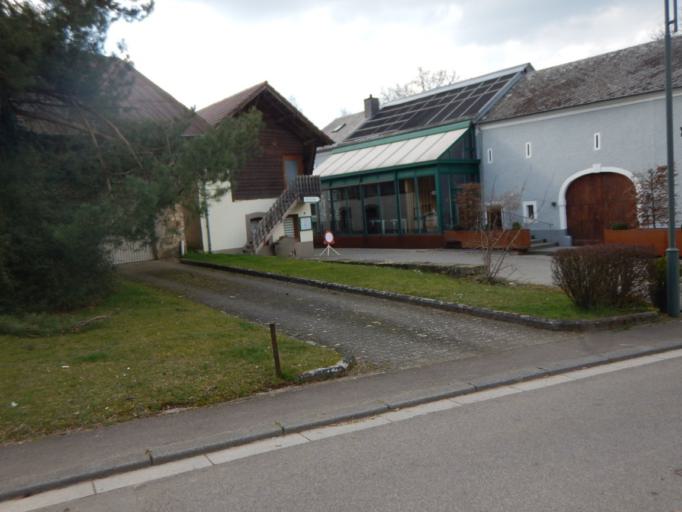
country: LU
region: Grevenmacher
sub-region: Canton d'Echternach
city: Beaufort
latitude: 49.8172
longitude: 6.2815
